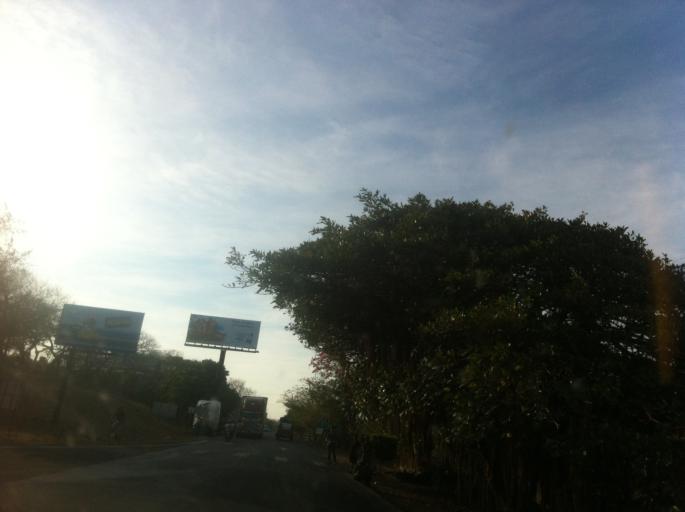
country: NI
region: Rivas
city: Rivas
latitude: 11.3544
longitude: -85.7416
